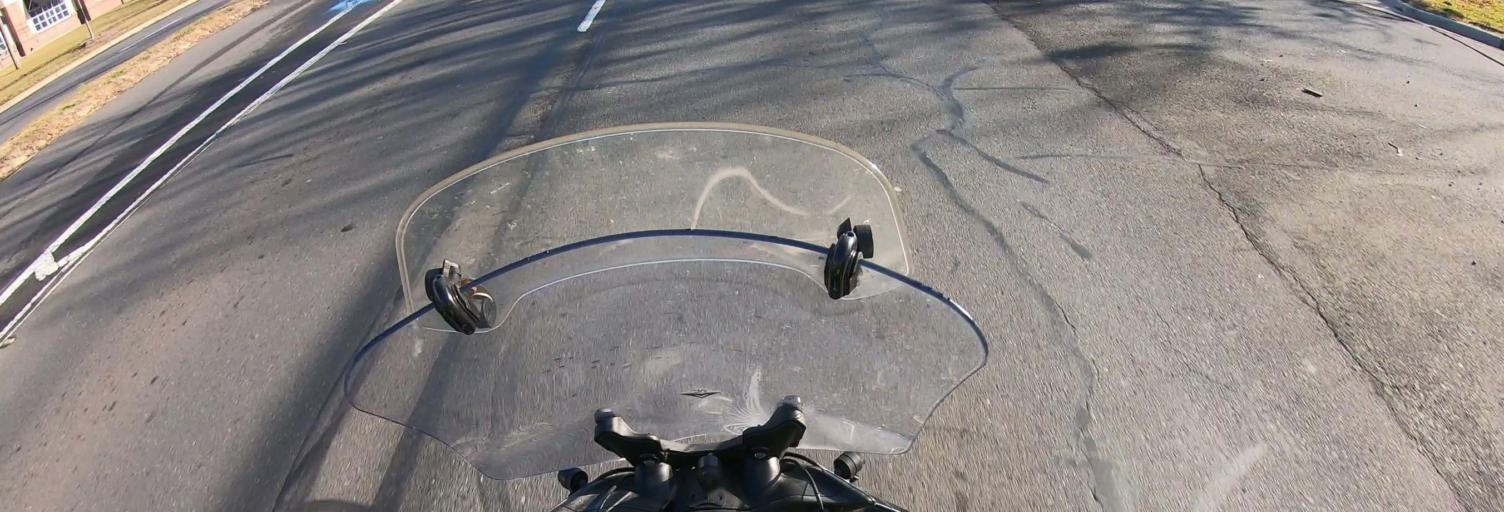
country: US
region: South Carolina
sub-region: York County
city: Lake Wylie
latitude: 35.1011
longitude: -80.9916
